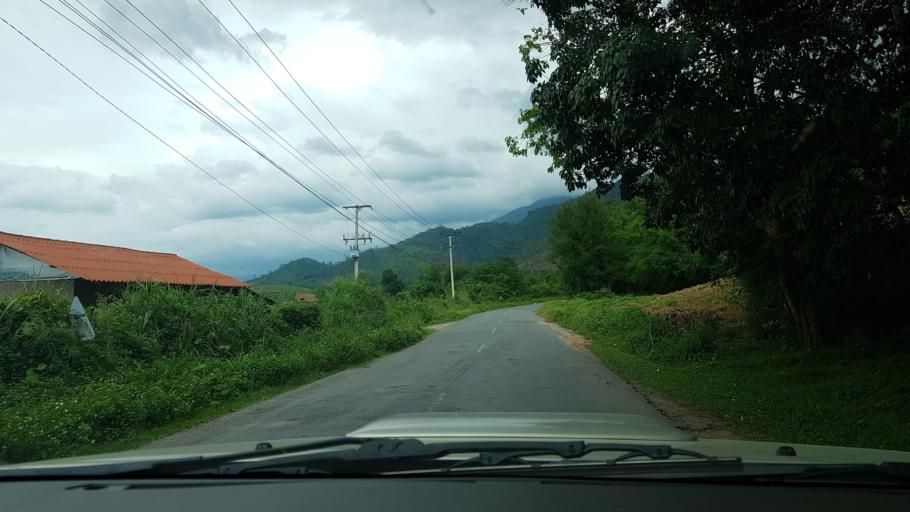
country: LA
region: Loungnamtha
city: Muang Nale
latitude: 20.3746
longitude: 101.7258
